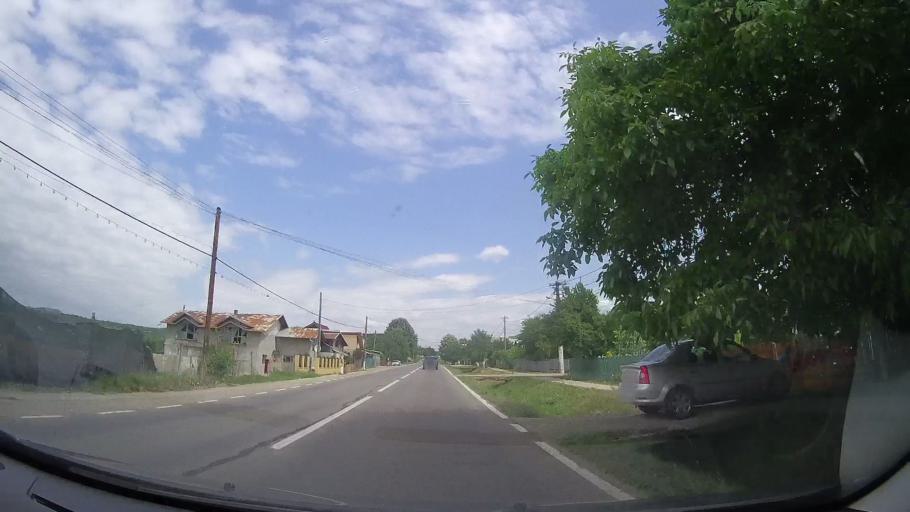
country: RO
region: Prahova
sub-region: Comuna Magurele
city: Magurele
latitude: 45.1050
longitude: 26.0355
